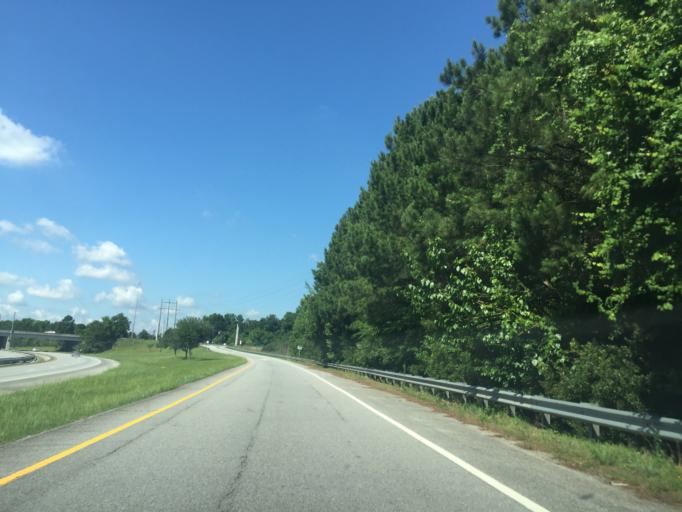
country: US
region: Georgia
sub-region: Chatham County
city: Garden City
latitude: 32.0415
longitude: -81.1621
